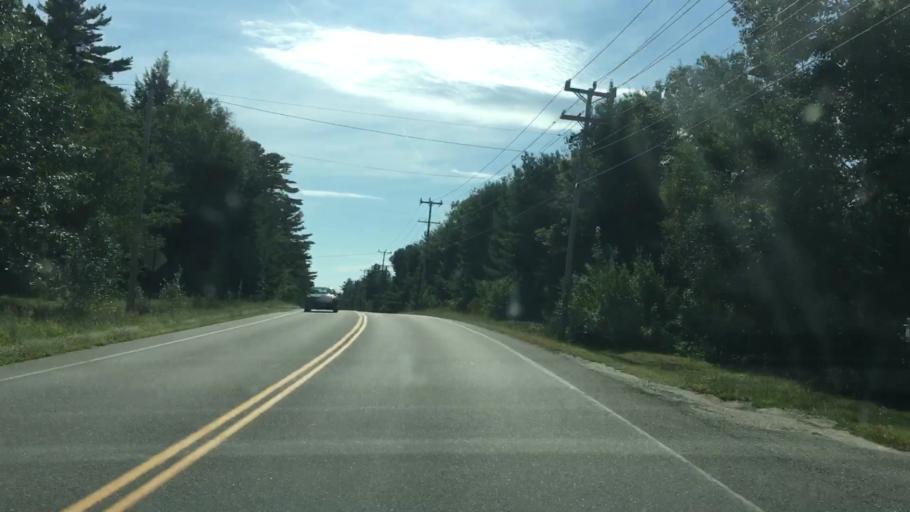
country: US
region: Maine
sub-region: Penobscot County
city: Lincoln
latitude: 45.3928
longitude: -68.5293
